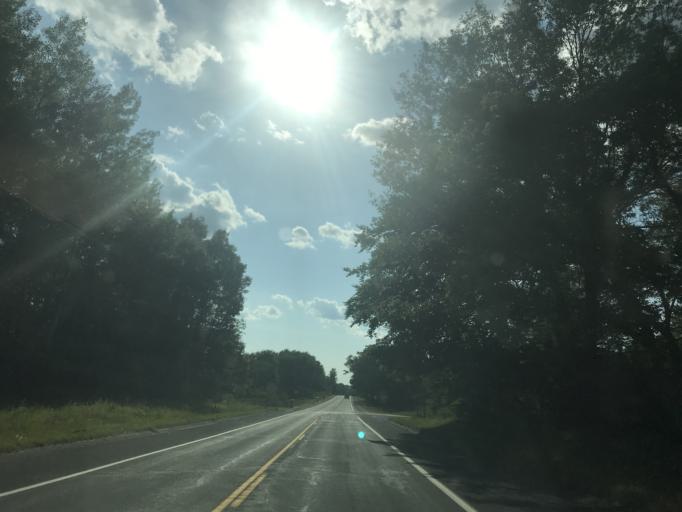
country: US
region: Michigan
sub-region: Newaygo County
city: White Cloud
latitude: 43.5682
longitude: -85.8002
